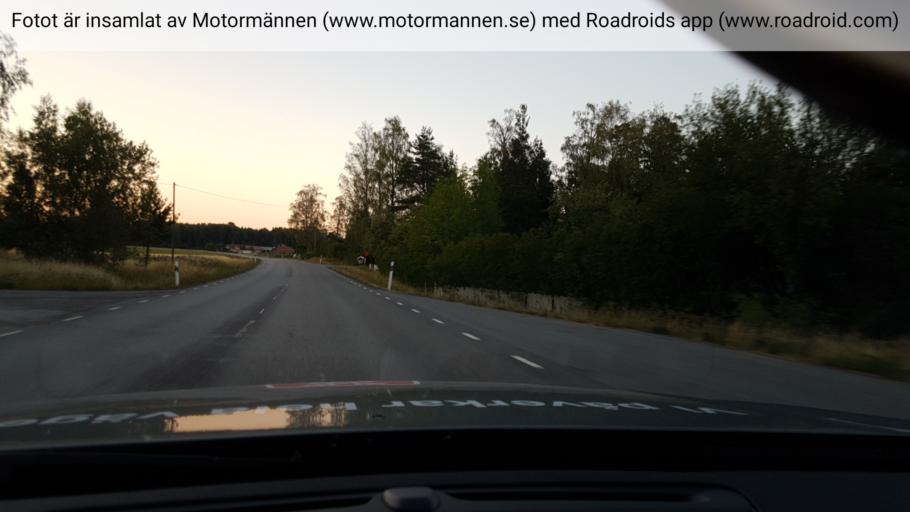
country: SE
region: Uppsala
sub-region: Heby Kommun
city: OEstervala
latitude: 60.1232
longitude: 17.2211
